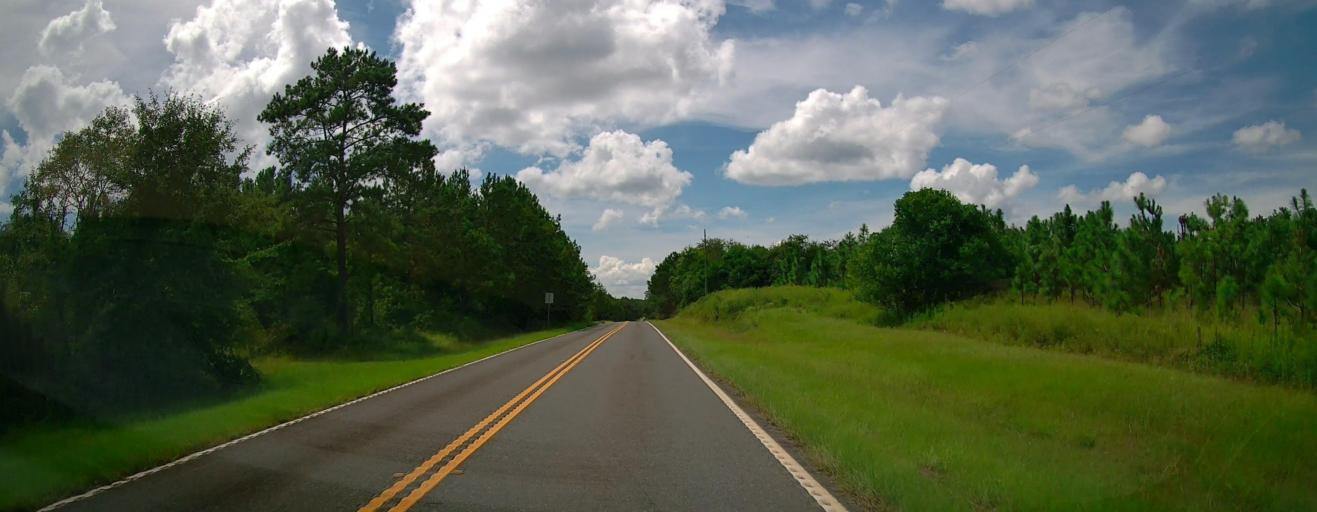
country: US
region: Georgia
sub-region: Taylor County
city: Butler
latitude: 32.4346
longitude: -84.1710
